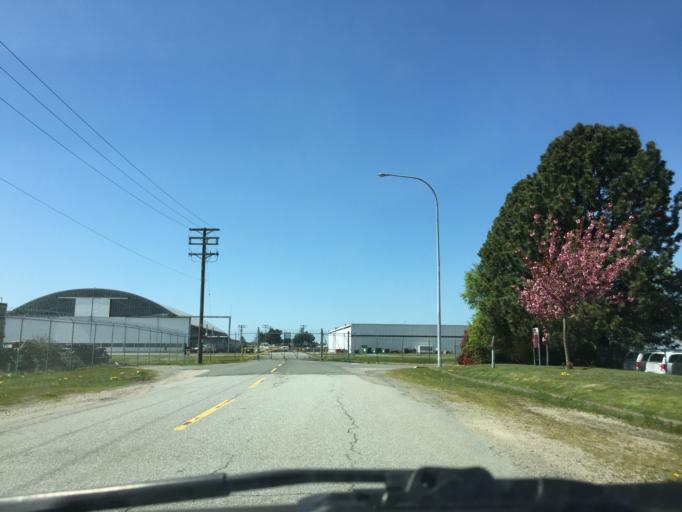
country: CA
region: British Columbia
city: Richmond
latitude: 49.1802
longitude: -123.1612
